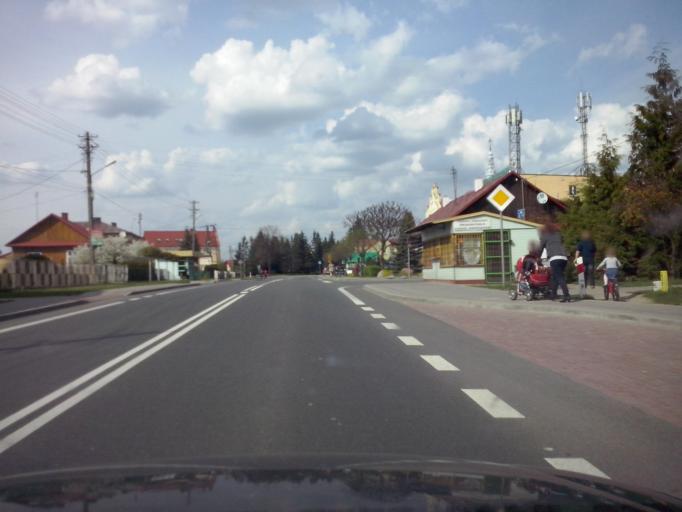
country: PL
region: Subcarpathian Voivodeship
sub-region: Powiat rzeszowski
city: Kamien
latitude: 50.3267
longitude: 22.1382
